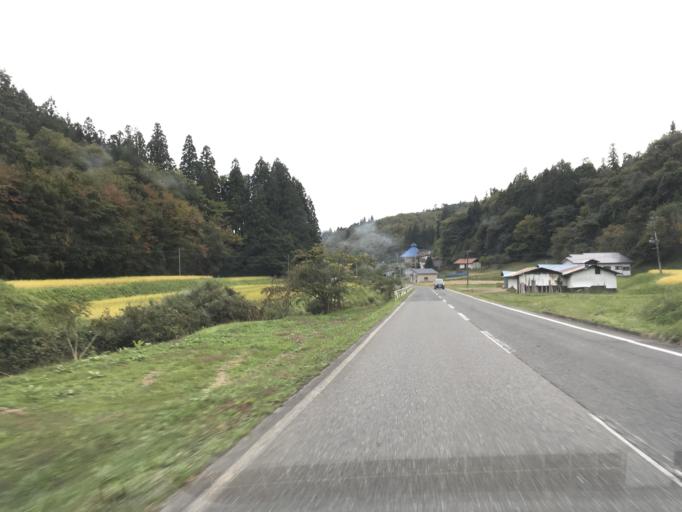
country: JP
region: Iwate
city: Mizusawa
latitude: 39.0432
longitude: 141.3303
